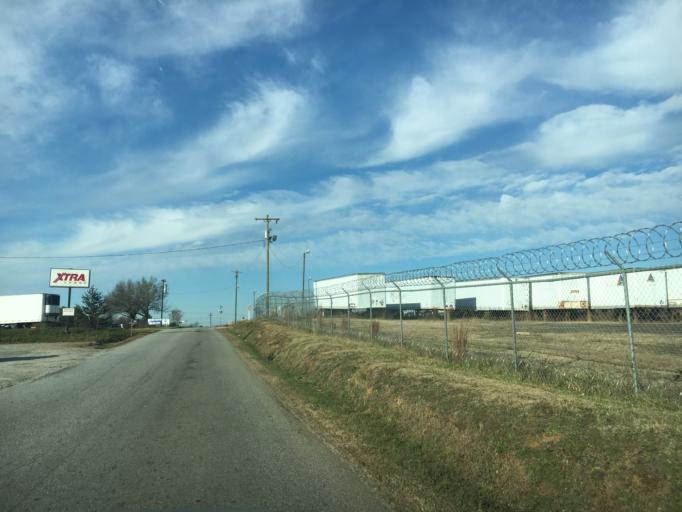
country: US
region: South Carolina
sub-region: Spartanburg County
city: Duncan
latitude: 34.8881
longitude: -82.1514
